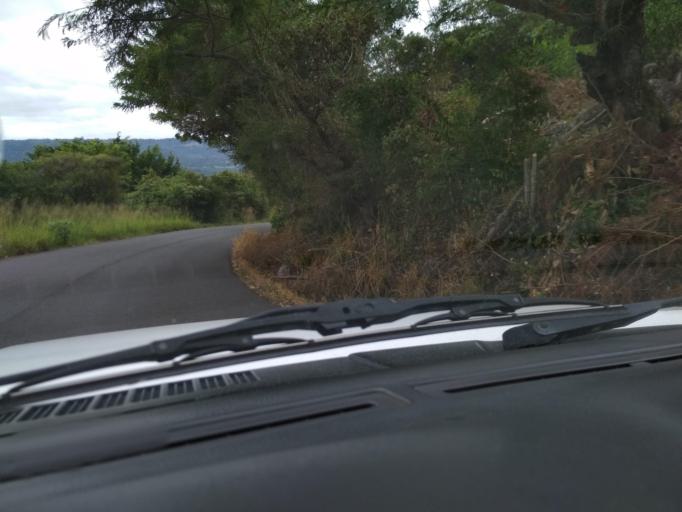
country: MX
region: Veracruz
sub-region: Actopan
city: Trapiche del Rosario
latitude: 19.5840
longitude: -96.7898
